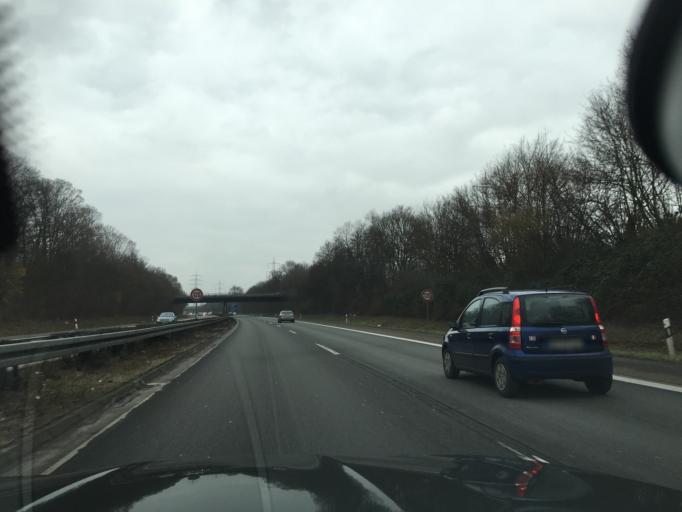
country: DE
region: North Rhine-Westphalia
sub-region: Regierungsbezirk Koln
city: Wahn-Heide
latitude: 50.8268
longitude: 7.0973
